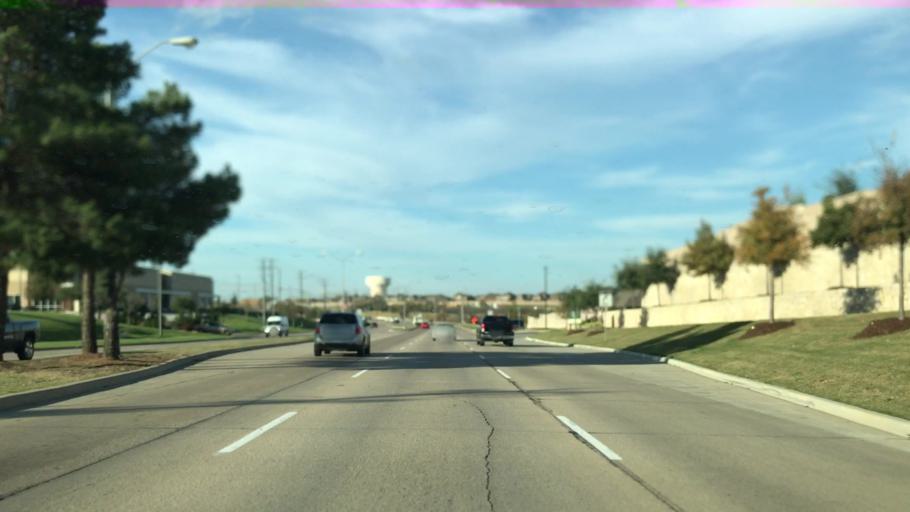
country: US
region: Texas
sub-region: Dallas County
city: Coppell
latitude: 32.8987
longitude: -96.9910
